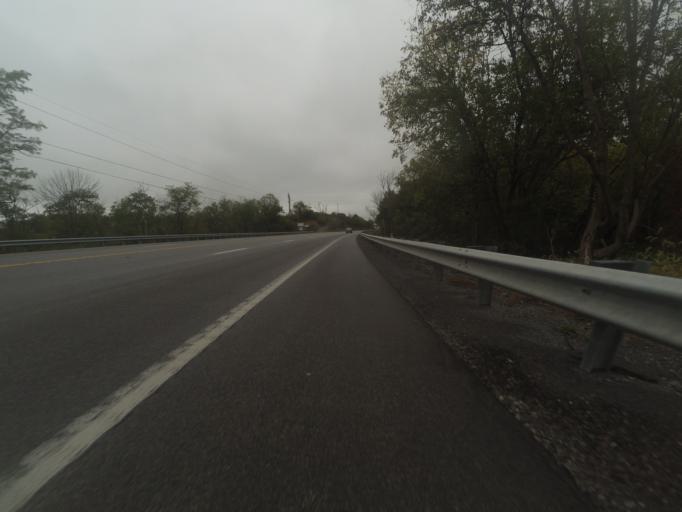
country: US
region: Pennsylvania
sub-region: Huntingdon County
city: McConnellstown
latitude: 40.5175
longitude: -78.0841
